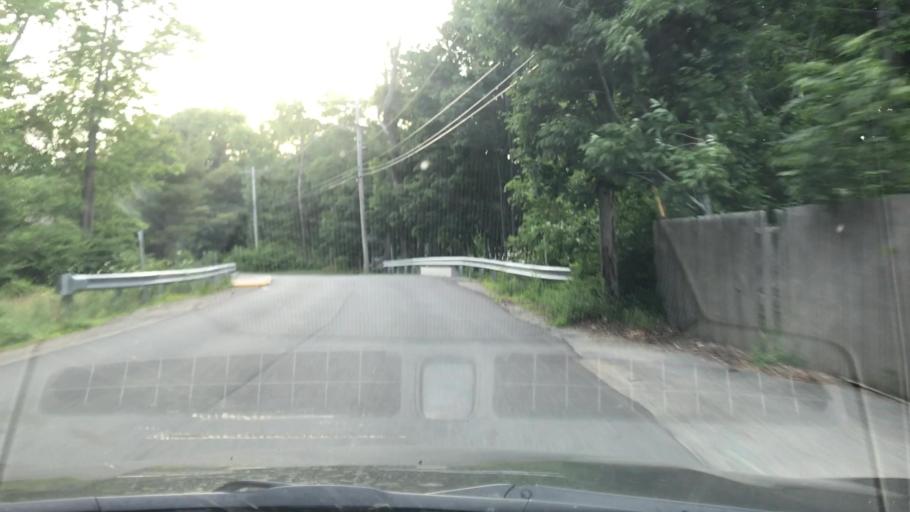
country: US
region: Maine
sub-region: Hancock County
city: Bar Harbor
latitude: 44.3803
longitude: -68.2043
